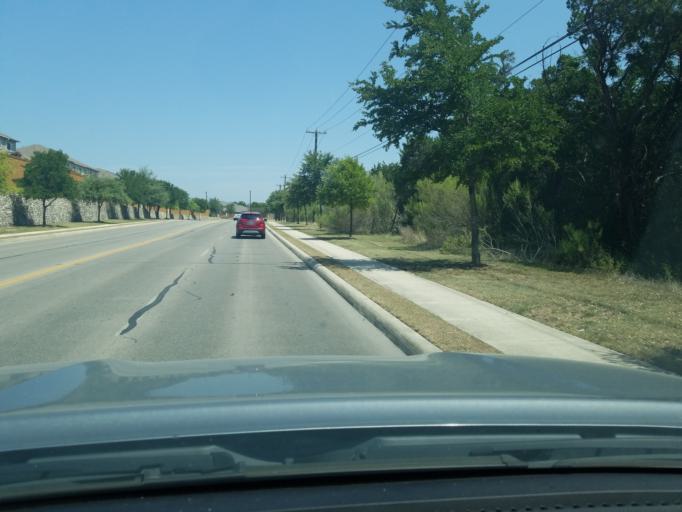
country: US
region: Texas
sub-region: Bexar County
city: Timberwood Park
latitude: 29.6982
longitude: -98.4814
